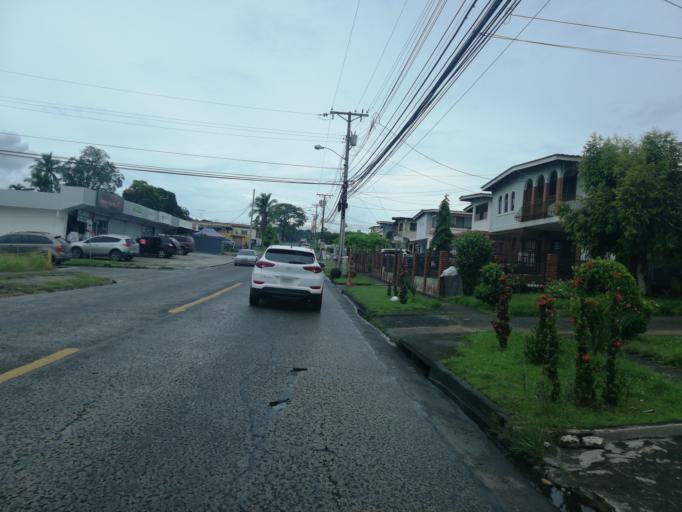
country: PA
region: Panama
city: Panama
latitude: 9.0106
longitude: -79.5381
